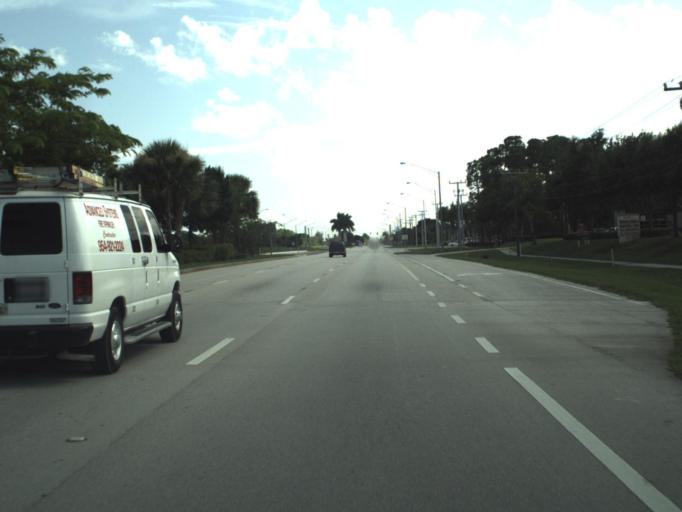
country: US
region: Florida
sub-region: Palm Beach County
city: Royal Palm Beach
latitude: 26.7073
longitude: -80.2011
